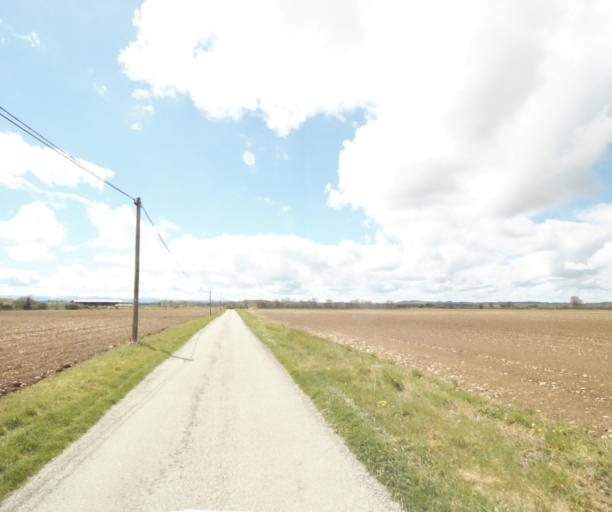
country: FR
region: Midi-Pyrenees
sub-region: Departement de l'Ariege
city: Saverdun
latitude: 43.2491
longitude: 1.6055
